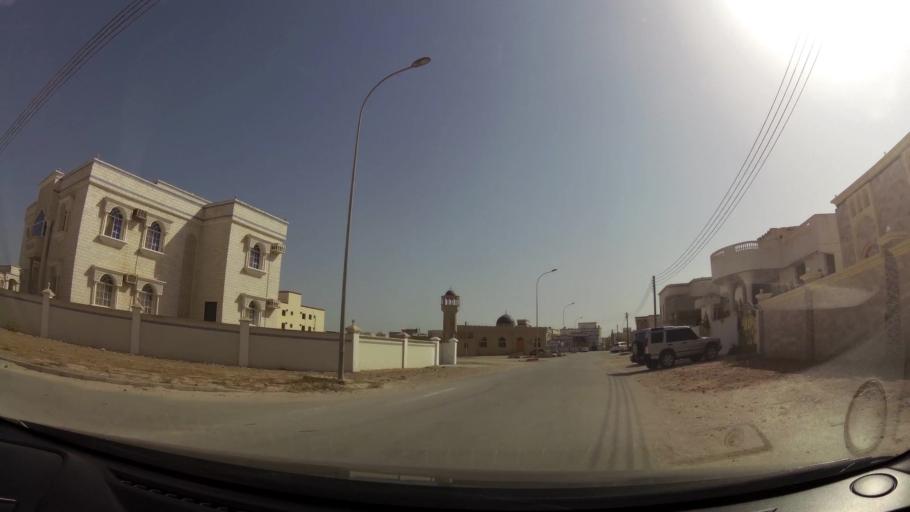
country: OM
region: Zufar
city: Salalah
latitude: 17.0082
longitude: 54.0120
